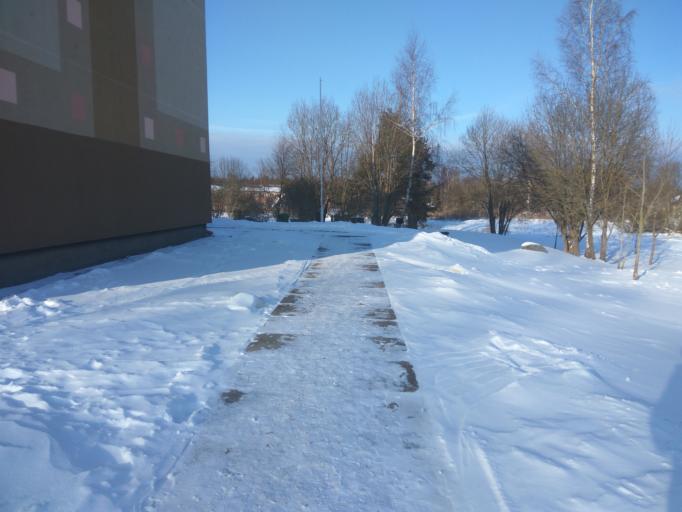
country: LV
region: Kuldigas Rajons
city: Kuldiga
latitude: 57.2778
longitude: 22.0184
